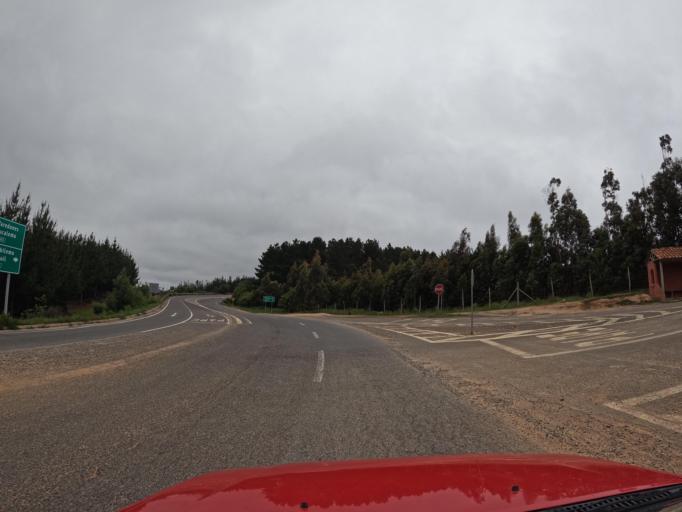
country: CL
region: O'Higgins
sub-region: Provincia de Colchagua
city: Santa Cruz
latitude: -34.6309
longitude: -72.0163
